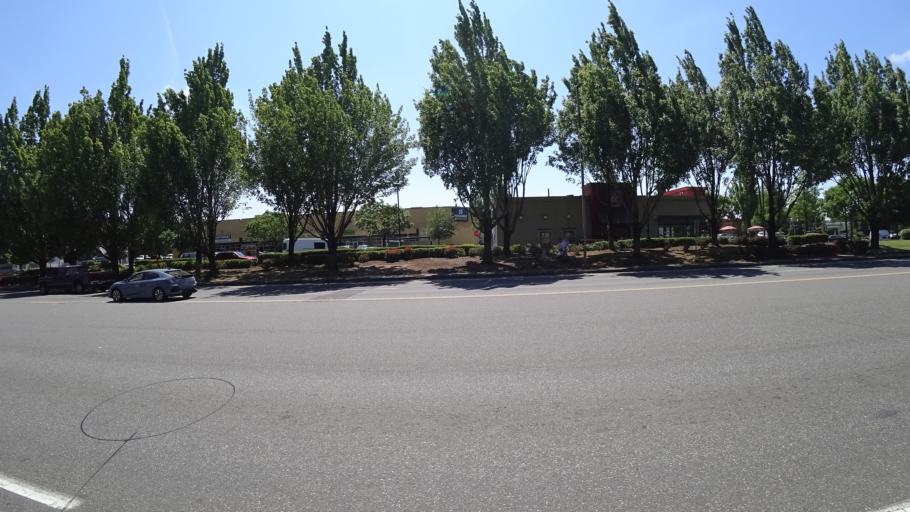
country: US
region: Washington
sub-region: Clark County
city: Mill Plain
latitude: 45.5652
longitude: -122.5324
